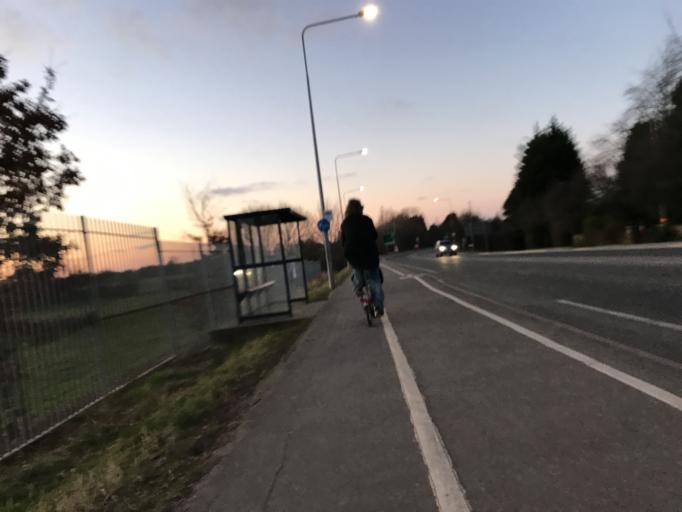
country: GB
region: England
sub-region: Lincolnshire
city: Holton le Clay
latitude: 53.5223
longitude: -0.0760
